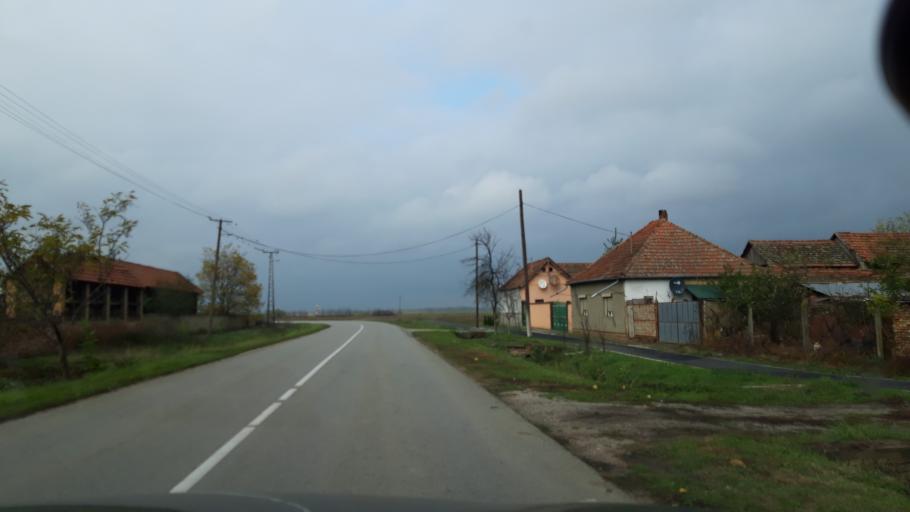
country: RS
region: Autonomna Pokrajina Vojvodina
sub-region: Severnobanatski Okrug
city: Kanjiza
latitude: 46.1296
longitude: 20.0935
